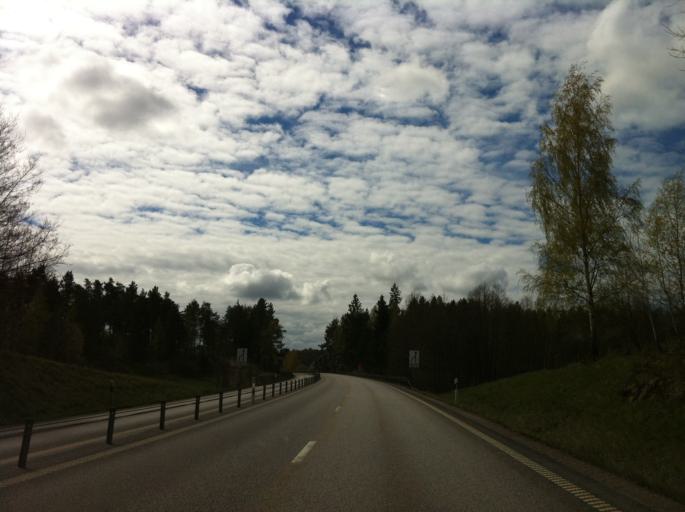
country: SE
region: OEstergoetland
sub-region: Valdemarsviks Kommun
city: Valdemarsvik
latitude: 58.1676
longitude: 16.5550
